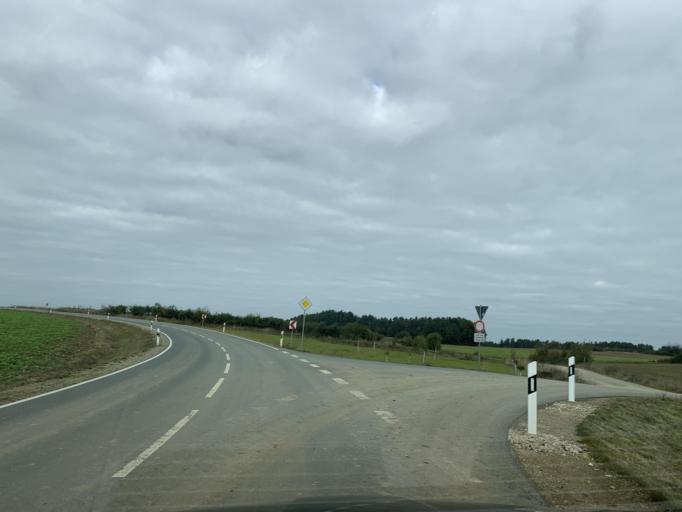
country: DE
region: Bavaria
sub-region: Upper Franconia
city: Aufsess
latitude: 49.8514
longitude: 11.2335
